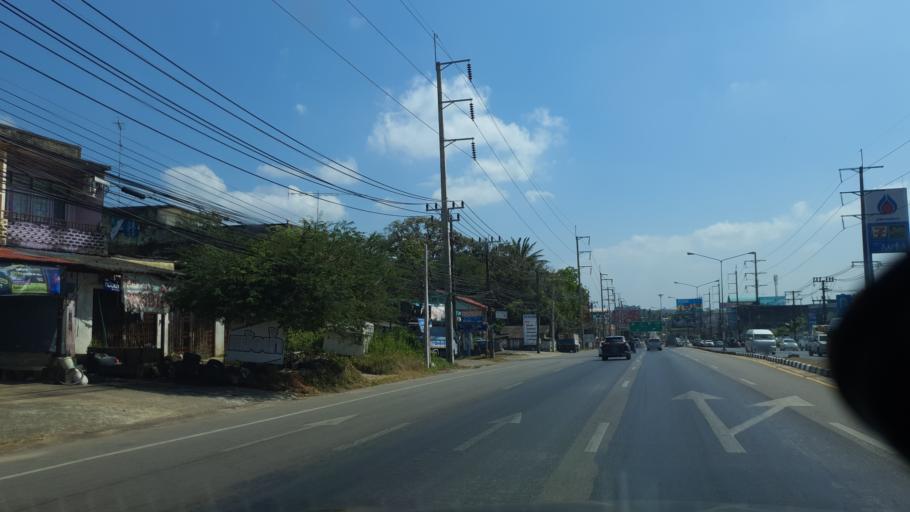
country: TH
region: Krabi
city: Krabi
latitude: 8.1027
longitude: 98.9042
